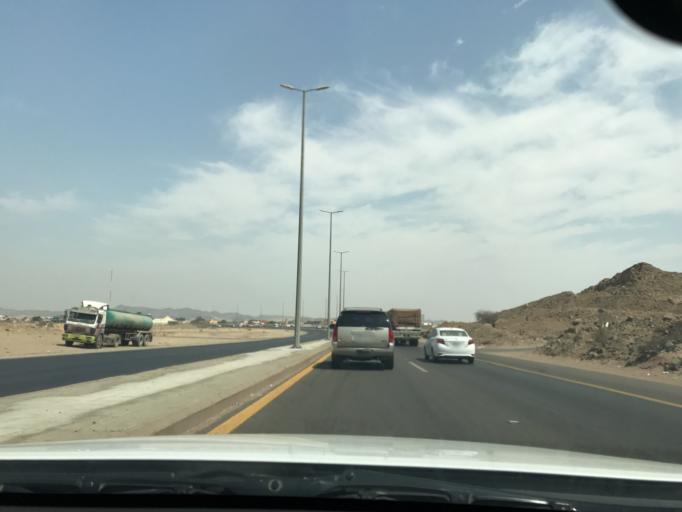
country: SA
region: Makkah
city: Jeddah
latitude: 21.4014
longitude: 39.4318
